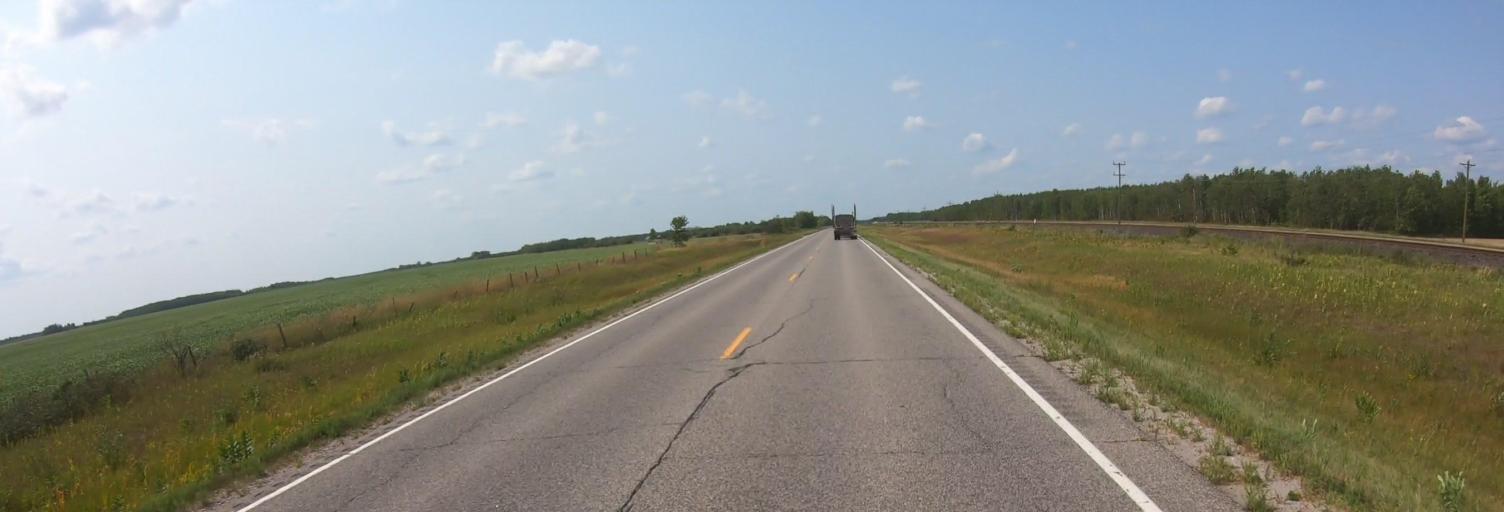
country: US
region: Minnesota
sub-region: Roseau County
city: Warroad
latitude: 48.8639
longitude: -95.2479
